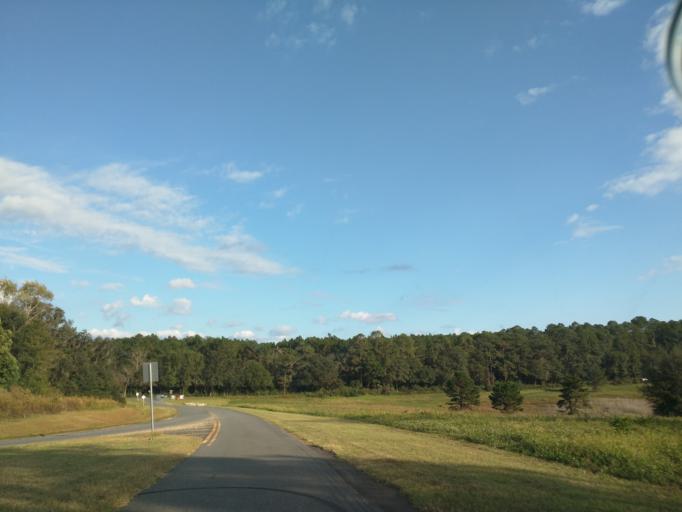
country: US
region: Florida
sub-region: Leon County
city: Tallahassee
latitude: 30.4107
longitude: -84.2127
